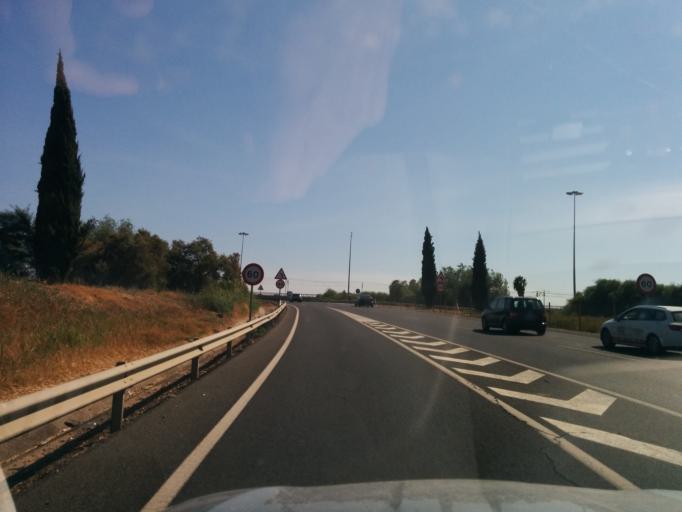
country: ES
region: Andalusia
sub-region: Provincia de Sevilla
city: San Juan de Aznalfarache
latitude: 37.3703
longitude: -6.0155
